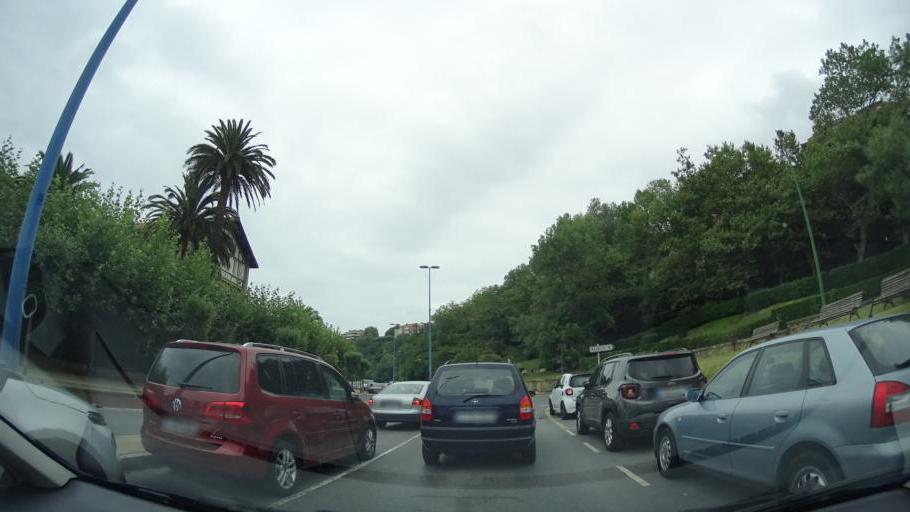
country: ES
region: Basque Country
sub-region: Bizkaia
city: Algorta
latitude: 43.3440
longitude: -3.0115
